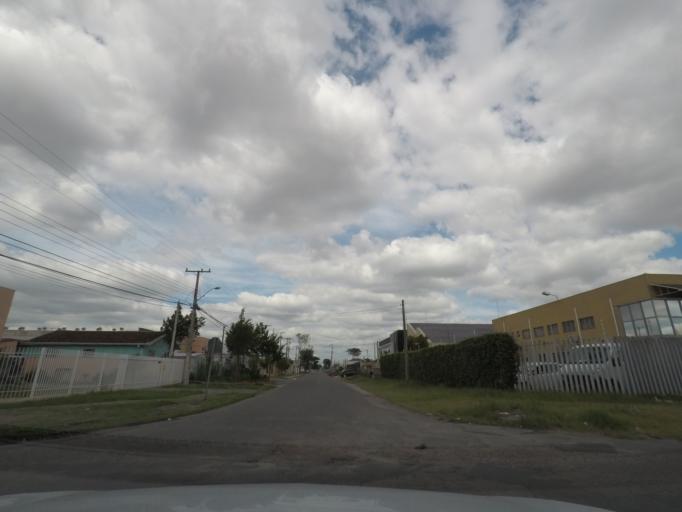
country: BR
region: Parana
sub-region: Sao Jose Dos Pinhais
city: Sao Jose dos Pinhais
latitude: -25.4865
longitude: -49.2395
